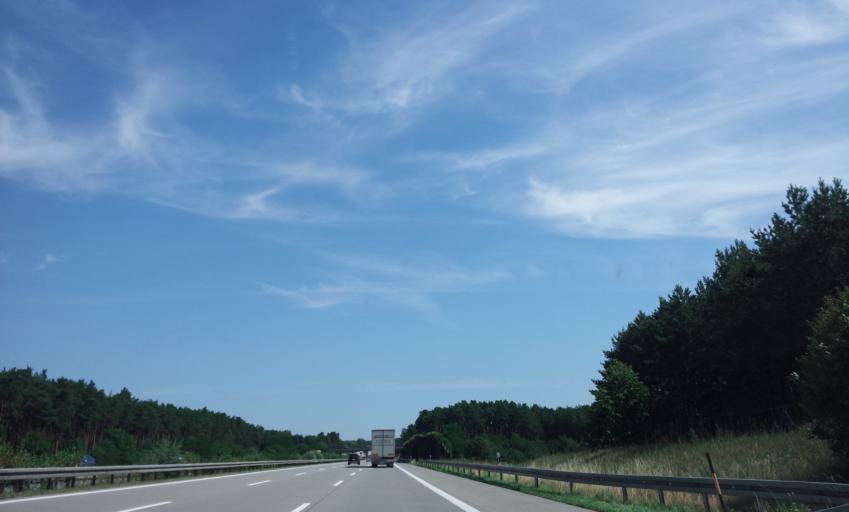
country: DE
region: Brandenburg
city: Erkner
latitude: 52.3729
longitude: 13.7694
